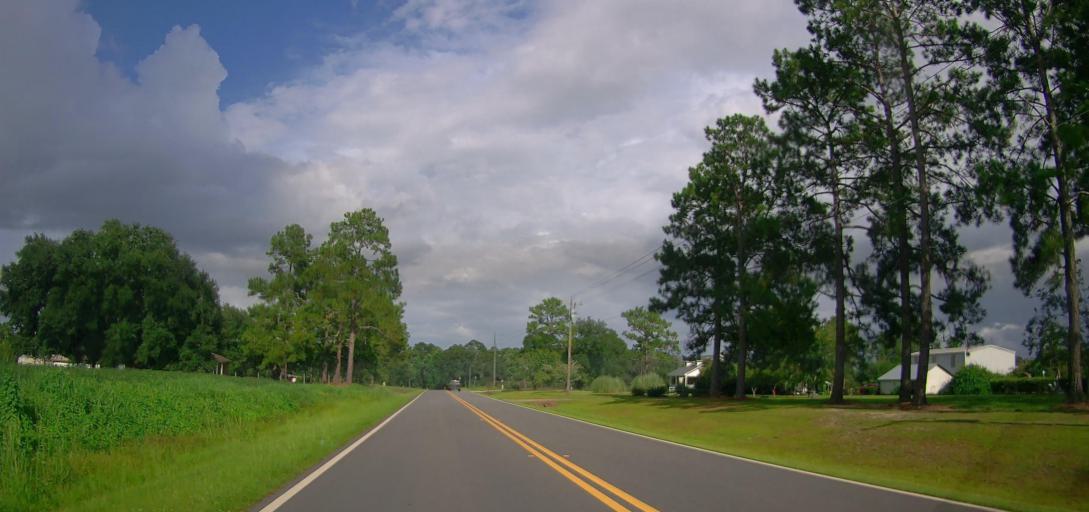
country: US
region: Georgia
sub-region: Coffee County
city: Douglas
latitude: 31.4484
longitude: -82.8727
